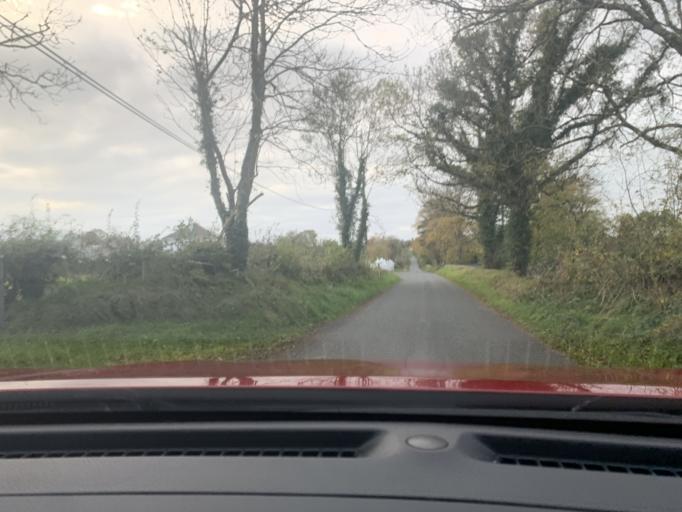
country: IE
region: Connaught
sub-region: Sligo
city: Tobercurry
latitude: 54.0239
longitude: -8.6454
